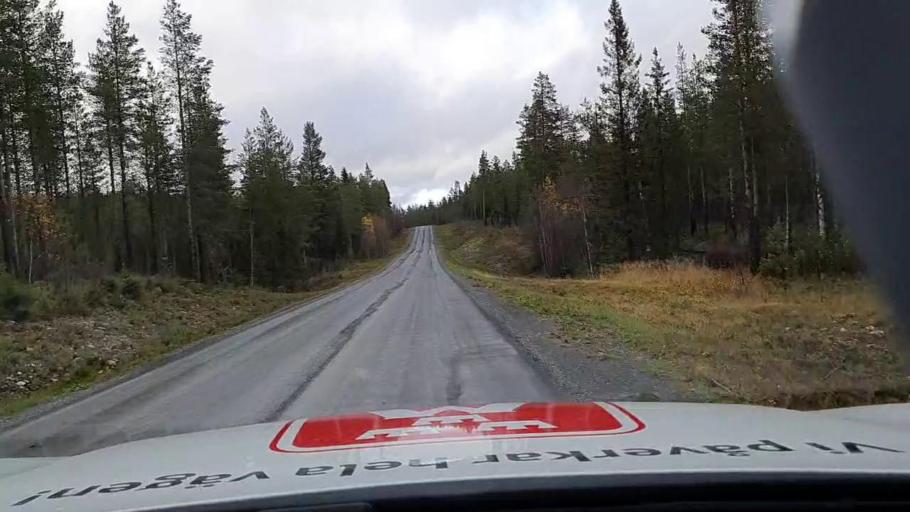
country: SE
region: Jaemtland
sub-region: Krokoms Kommun
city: Valla
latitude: 63.0729
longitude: 13.9591
